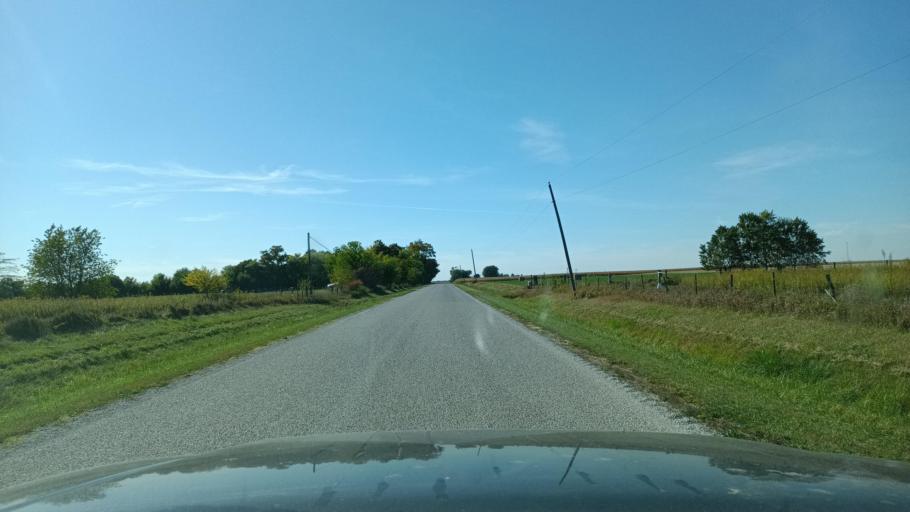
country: US
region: Illinois
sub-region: Logan County
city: Atlanta
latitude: 40.2435
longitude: -89.1946
